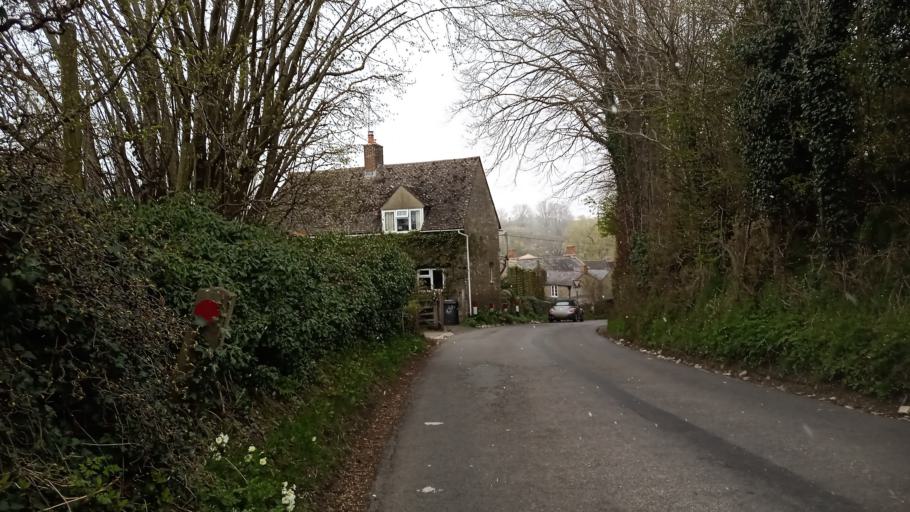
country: GB
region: England
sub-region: Oxfordshire
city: Witney
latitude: 51.8046
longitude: -1.5064
